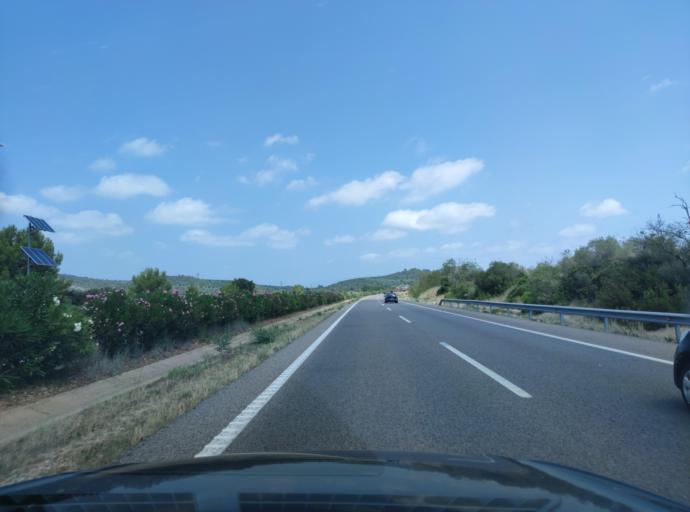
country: ES
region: Catalonia
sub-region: Provincia de Tarragona
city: Santa Barbara
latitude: 40.6573
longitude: 0.5102
